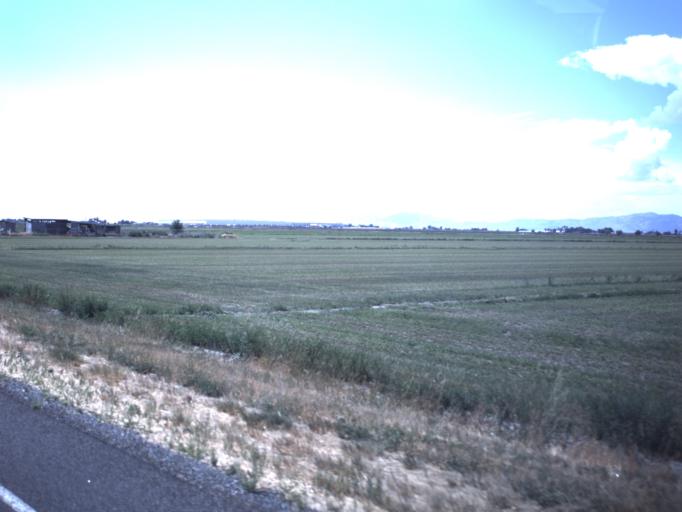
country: US
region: Utah
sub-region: Box Elder County
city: Honeyville
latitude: 41.5779
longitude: -112.1297
